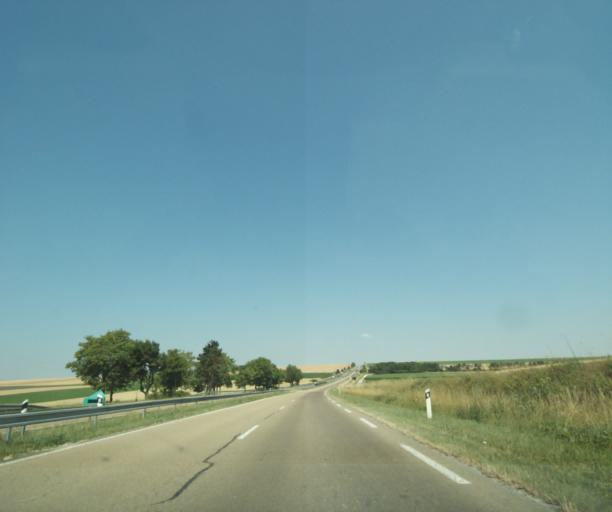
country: FR
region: Champagne-Ardenne
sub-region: Departement de la Marne
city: Fagnieres
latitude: 49.0409
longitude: 4.3107
